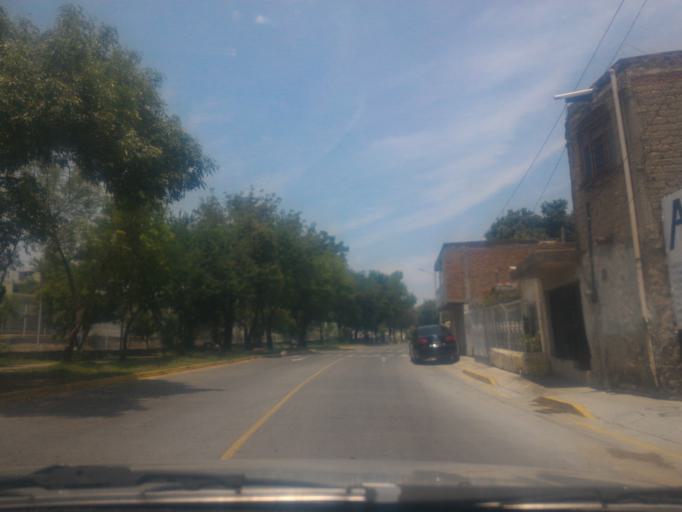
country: MX
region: Jalisco
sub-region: Tlajomulco de Zuniga
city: Altus Bosques
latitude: 20.6202
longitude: -103.3679
